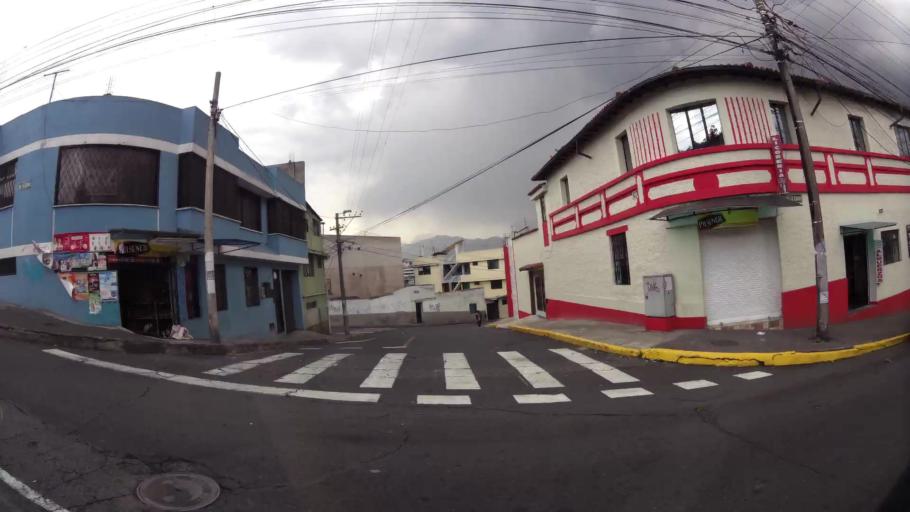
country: EC
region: Pichincha
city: Quito
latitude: -0.2470
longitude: -78.5090
